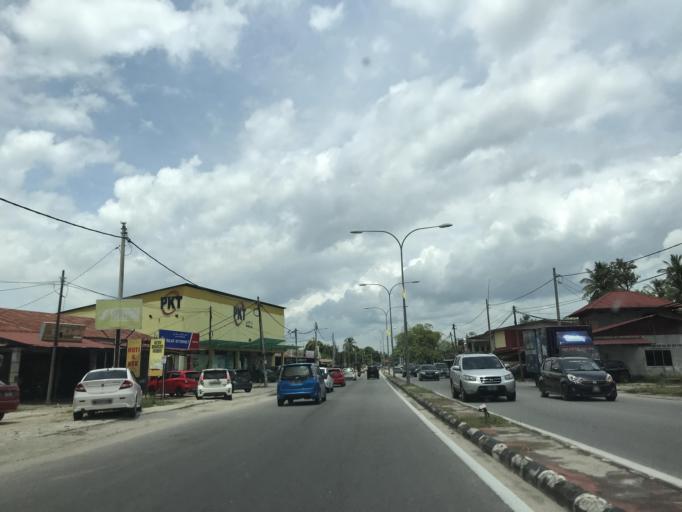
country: MY
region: Kelantan
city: Pasir Mas
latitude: 6.0660
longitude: 102.2056
